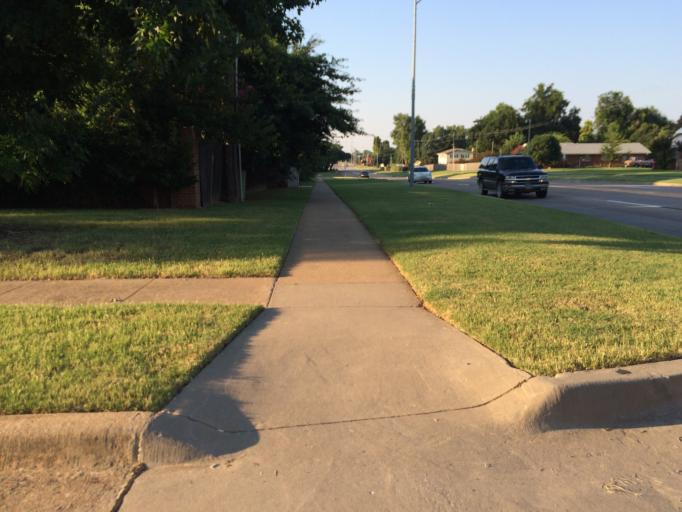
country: US
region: Oklahoma
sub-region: Cleveland County
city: Norman
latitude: 35.2161
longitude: -97.4765
